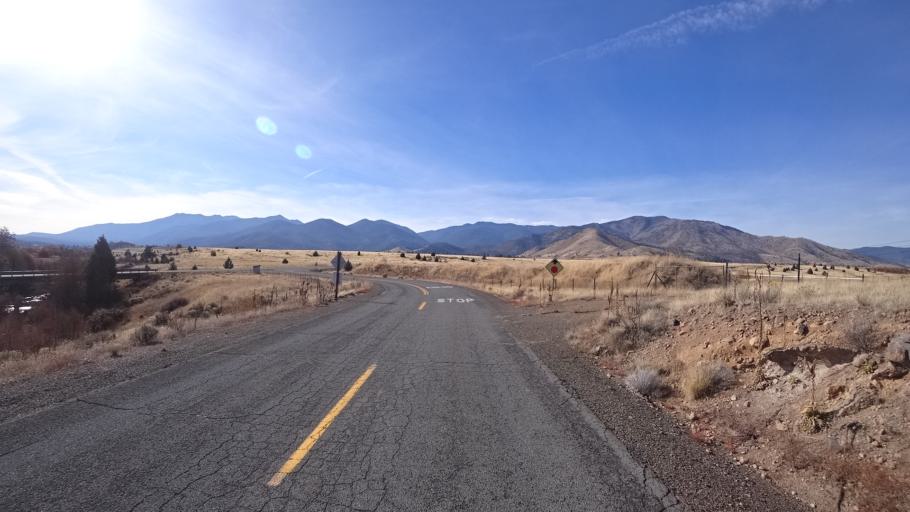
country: US
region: California
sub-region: Siskiyou County
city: Weed
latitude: 41.4718
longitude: -122.4410
